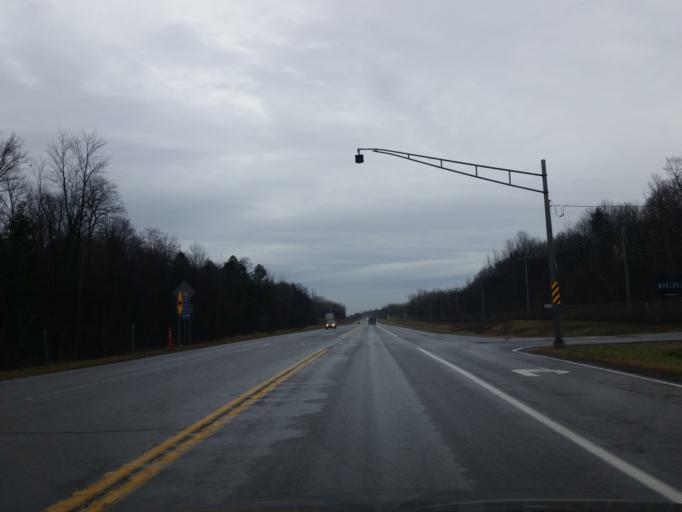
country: CA
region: Quebec
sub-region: Laurentides
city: Mirabel
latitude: 45.6842
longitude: -74.0795
